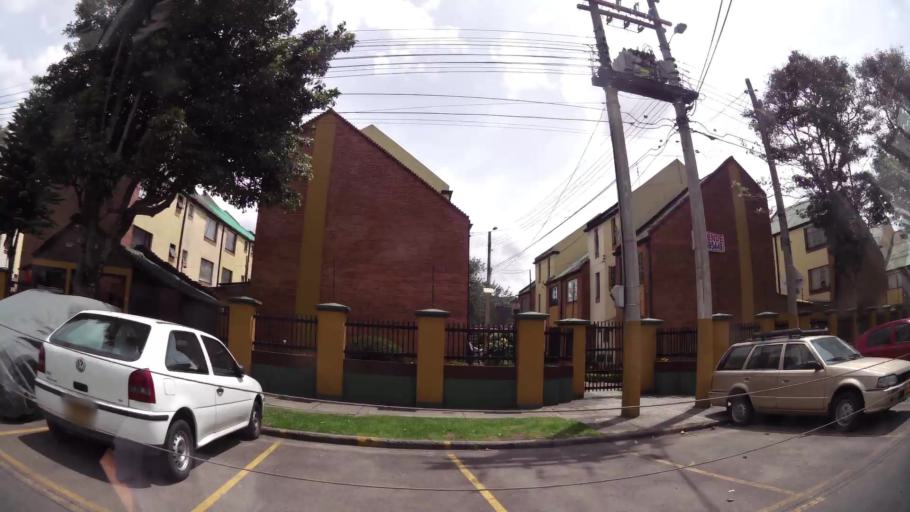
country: CO
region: Cundinamarca
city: Funza
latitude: 4.7106
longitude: -74.1139
